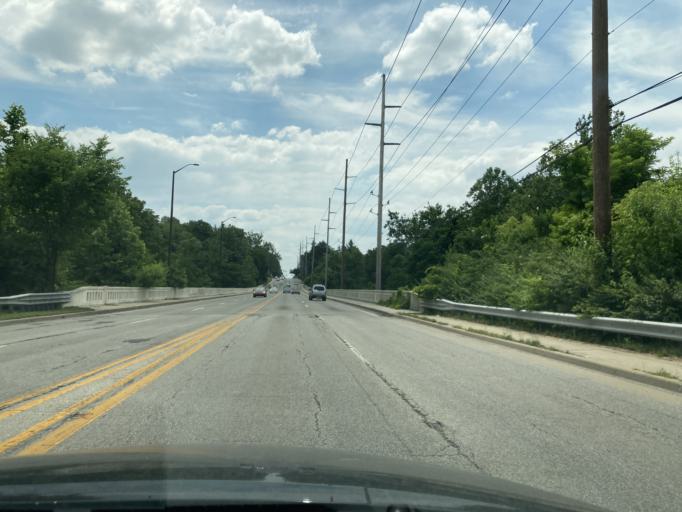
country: US
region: Indiana
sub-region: Marion County
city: Broad Ripple
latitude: 39.8333
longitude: -86.1849
